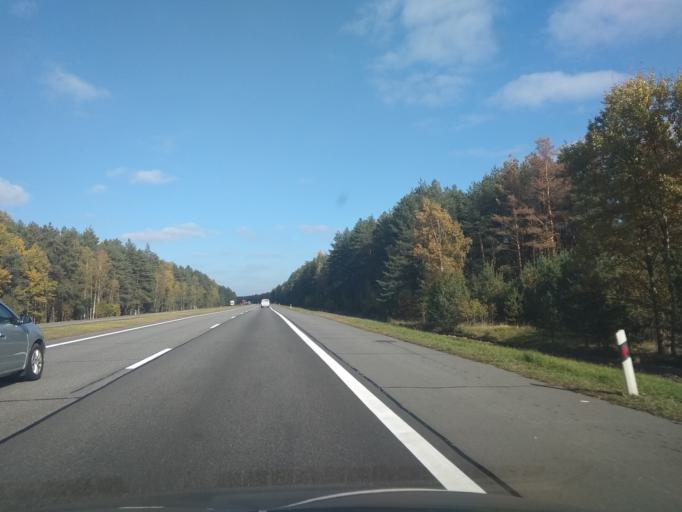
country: BY
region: Brest
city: Baranovichi
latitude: 53.0614
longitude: 25.8692
